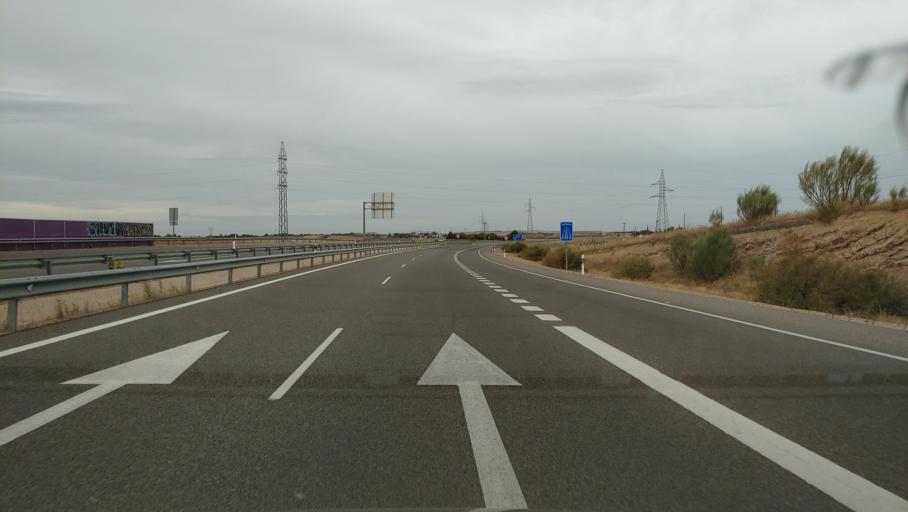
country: ES
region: Castille-La Mancha
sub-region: Provincia de Ciudad Real
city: Miguelturra
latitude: 38.9471
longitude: -3.8792
